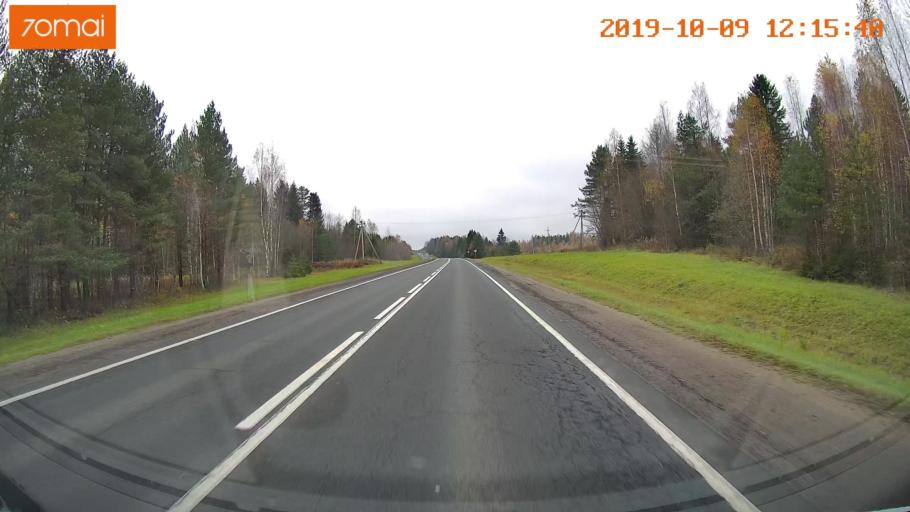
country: RU
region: Jaroslavl
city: Prechistoye
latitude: 58.4801
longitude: 40.3229
